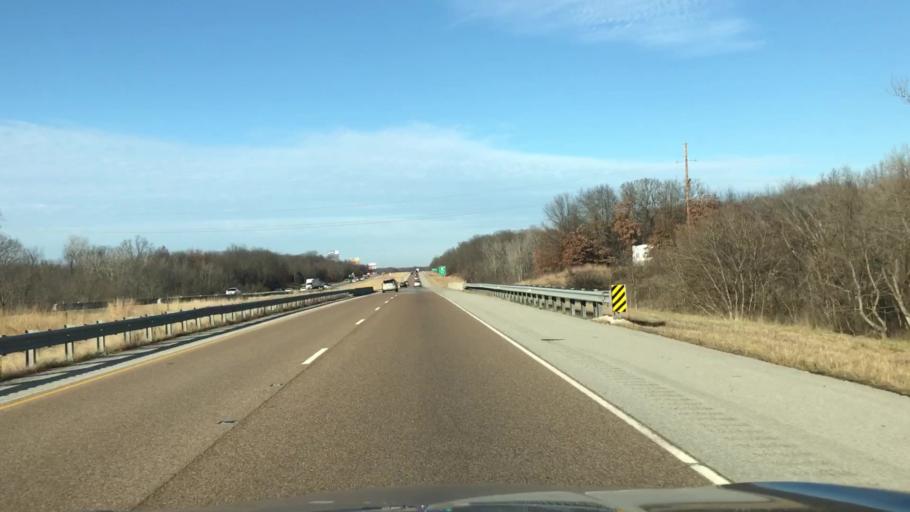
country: US
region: Illinois
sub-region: Macoupin County
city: Mount Olive
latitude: 39.0568
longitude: -89.7555
